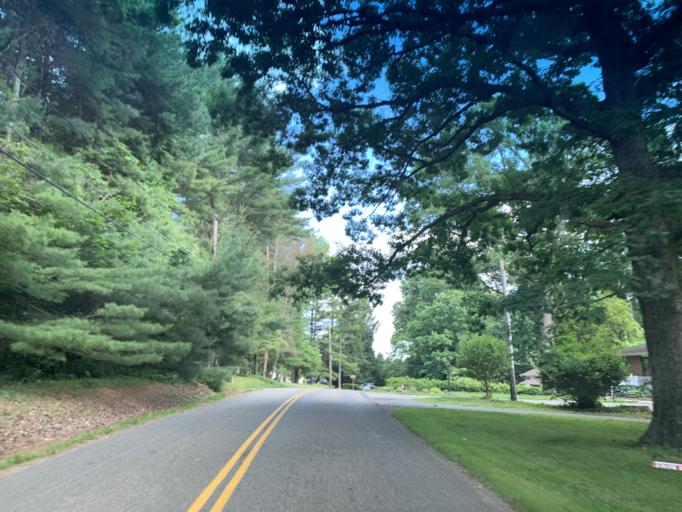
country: US
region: Maryland
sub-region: Harford County
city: Jarrettsville
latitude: 39.5582
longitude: -76.4479
